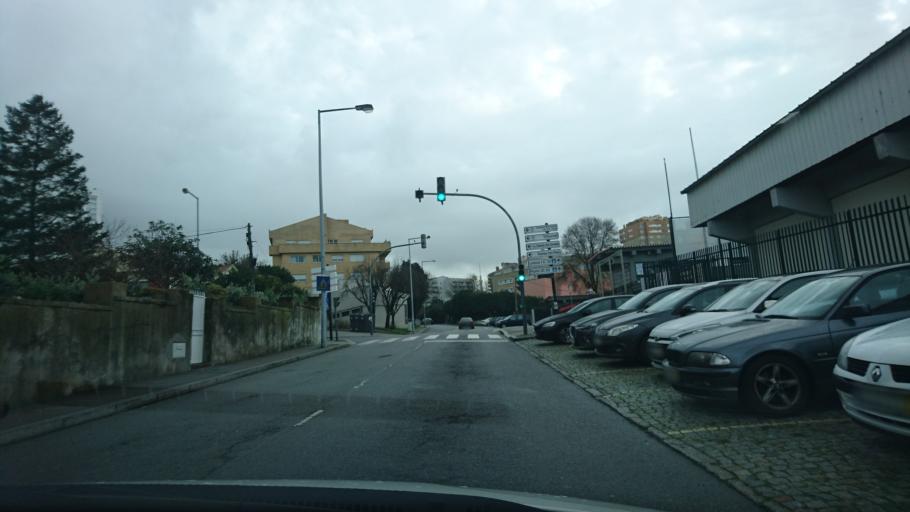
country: PT
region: Porto
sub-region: Vila Nova de Gaia
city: Vila Nova de Gaia
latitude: 41.1240
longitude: -8.6196
